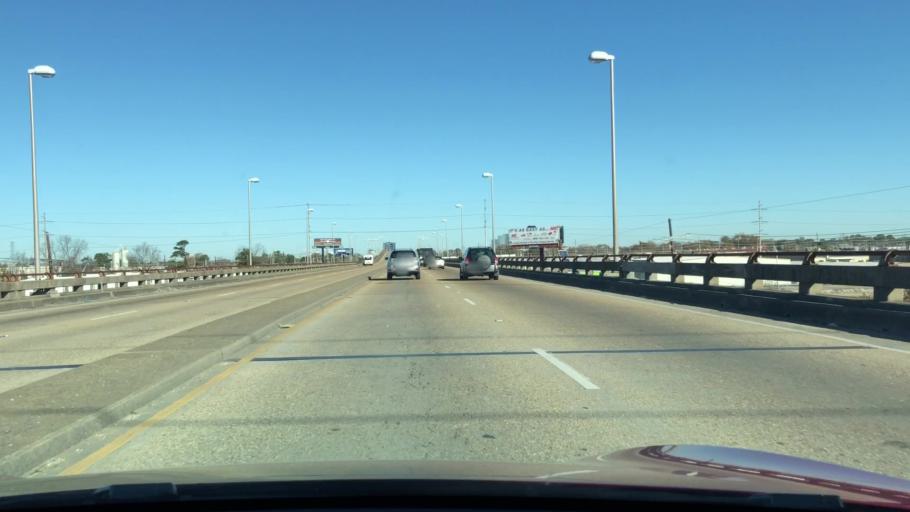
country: US
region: Louisiana
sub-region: Jefferson Parish
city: Jefferson
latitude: 29.9700
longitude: -90.1565
